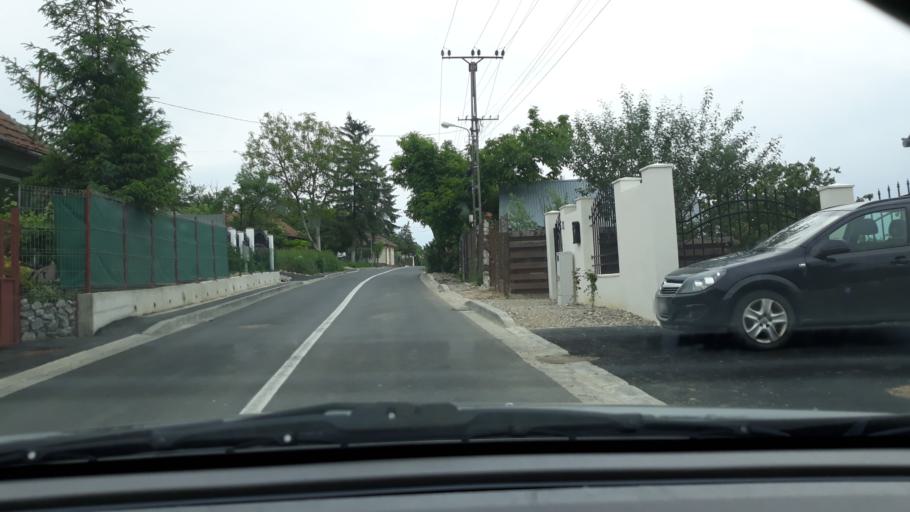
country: RO
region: Bihor
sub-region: Comuna Osorheiu
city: Osorheiu
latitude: 47.0587
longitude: 22.0115
